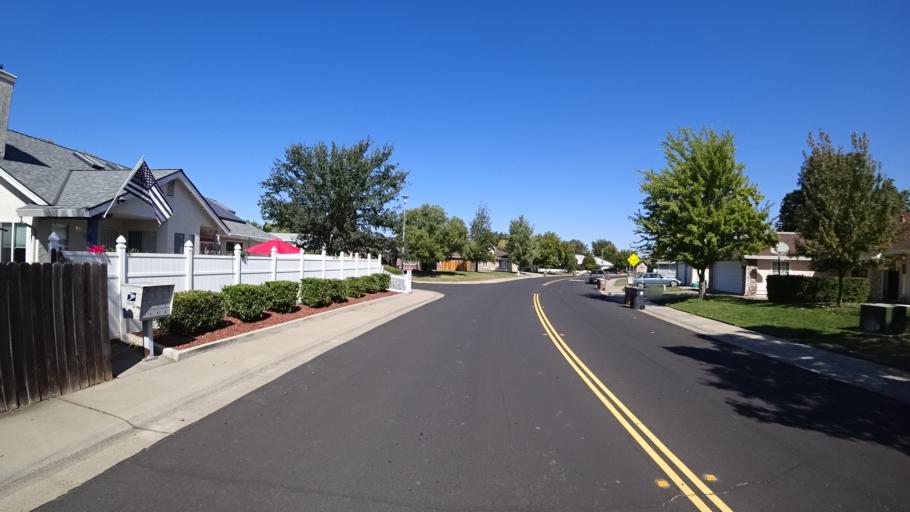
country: US
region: California
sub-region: Sacramento County
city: Laguna
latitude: 38.4362
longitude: -121.4329
